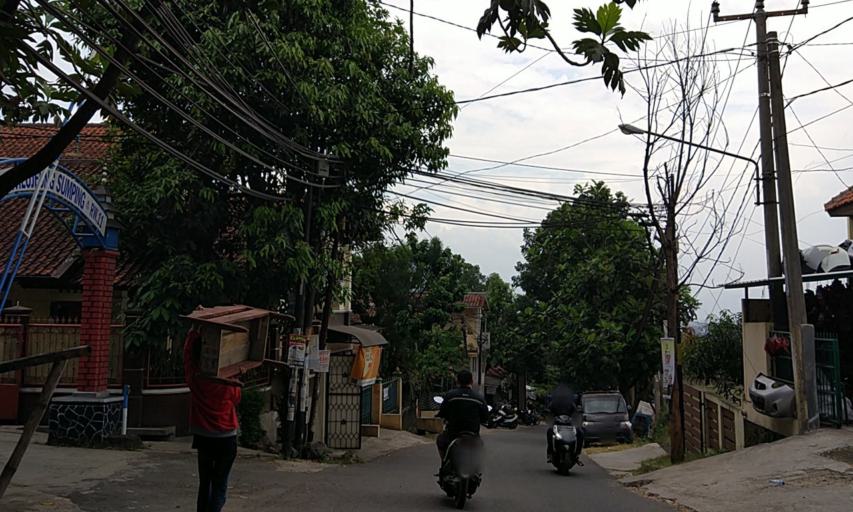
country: ID
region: West Java
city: Cileunyi
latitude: -6.9021
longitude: 107.6979
